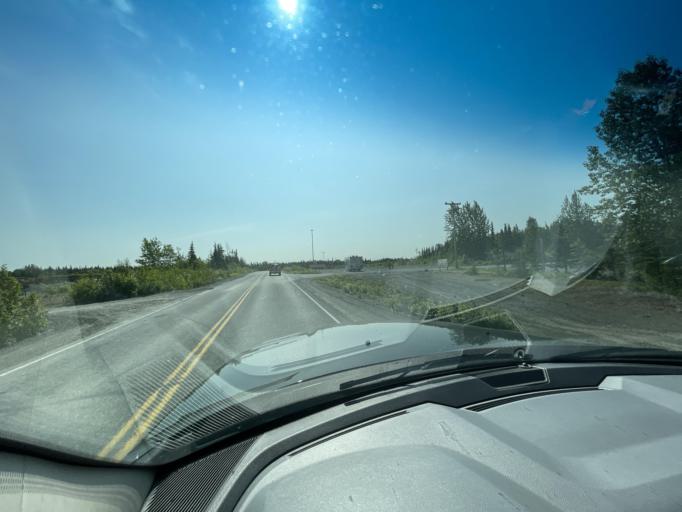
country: US
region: Alaska
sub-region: Kenai Peninsula Borough
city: Cohoe
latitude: 60.2988
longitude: -151.2801
